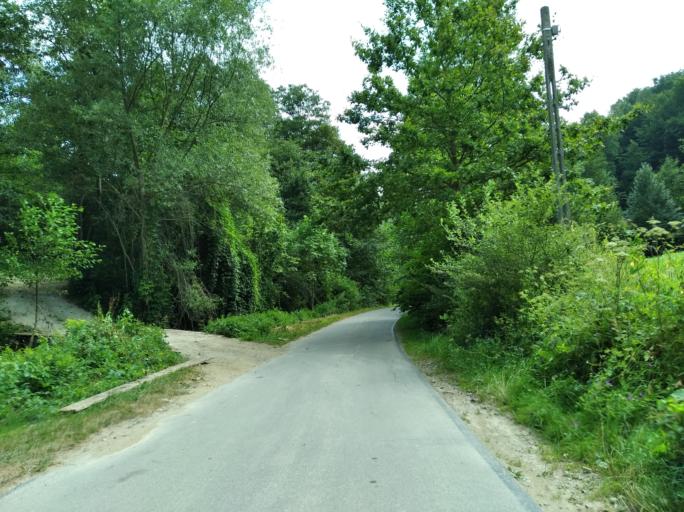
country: PL
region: Subcarpathian Voivodeship
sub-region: Powiat krosnienski
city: Wojaszowka
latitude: 49.7858
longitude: 21.6982
